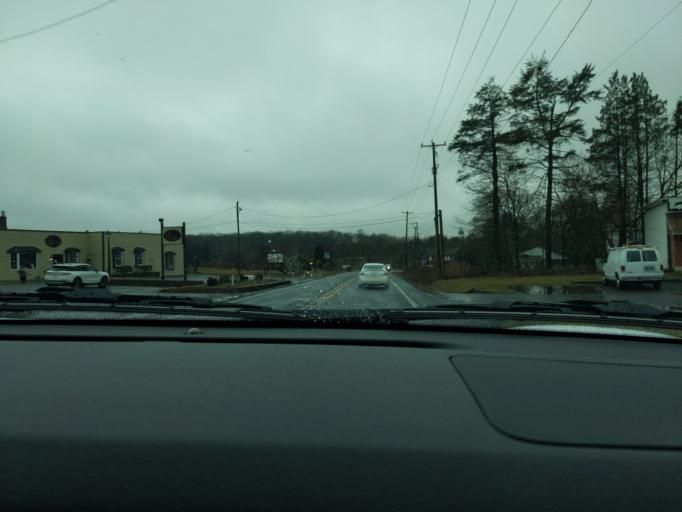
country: US
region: Pennsylvania
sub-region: Bucks County
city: Dublin
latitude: 40.3632
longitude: -75.1882
